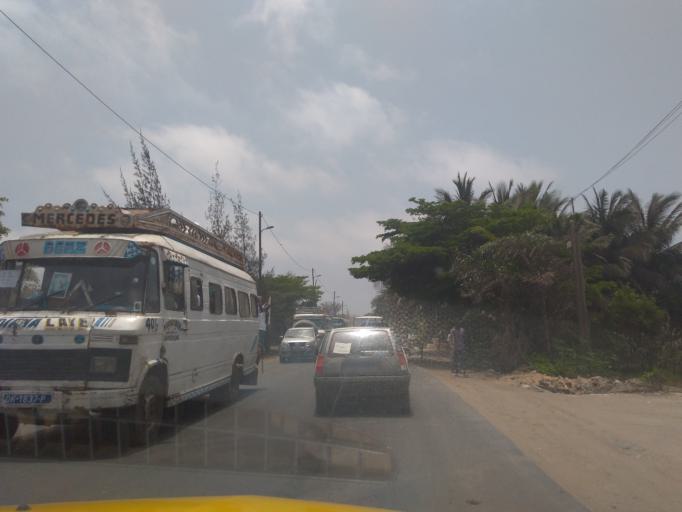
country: SN
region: Dakar
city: Pikine
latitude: 14.7480
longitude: -17.4259
